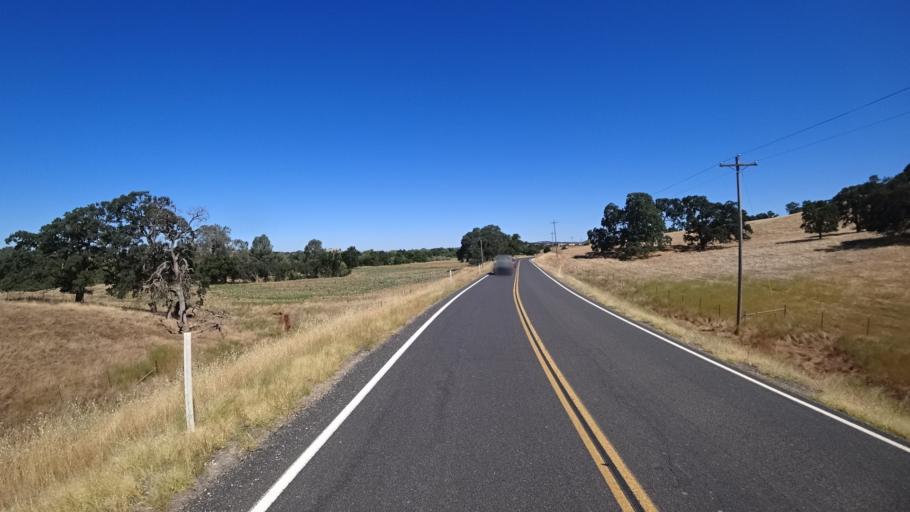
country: US
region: California
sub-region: Calaveras County
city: Rancho Calaveras
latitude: 38.0808
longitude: -120.8726
